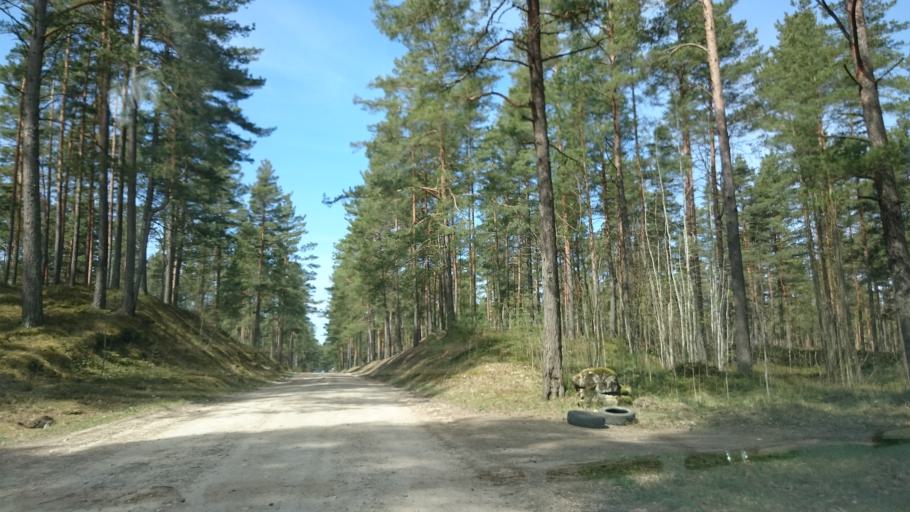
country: LV
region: Carnikava
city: Carnikava
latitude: 57.1727
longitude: 24.3473
